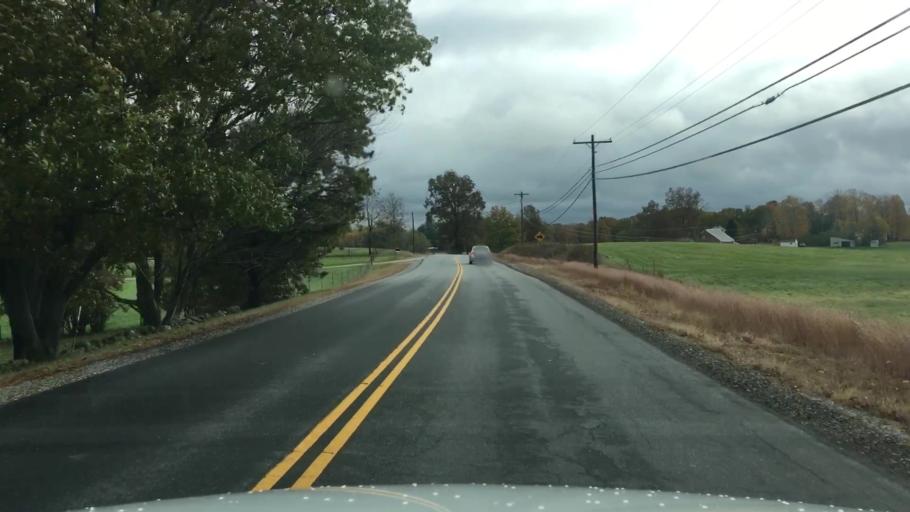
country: US
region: New Hampshire
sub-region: Strafford County
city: Lee
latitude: 43.1054
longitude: -70.9937
